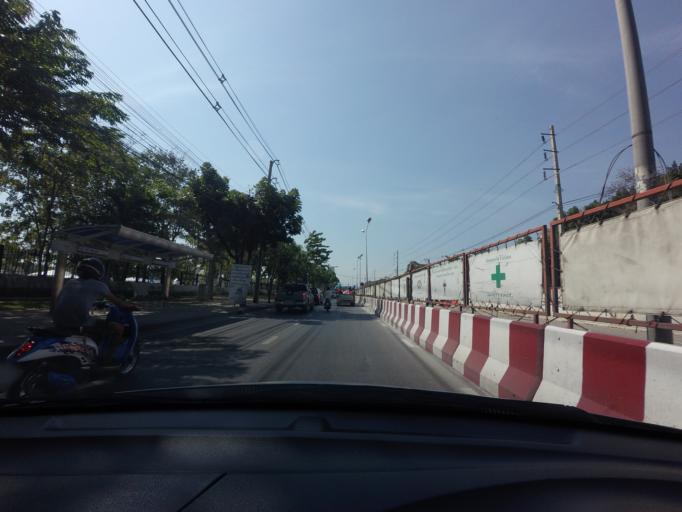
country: TH
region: Bangkok
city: Sai Mai
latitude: 13.9224
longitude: 100.6244
